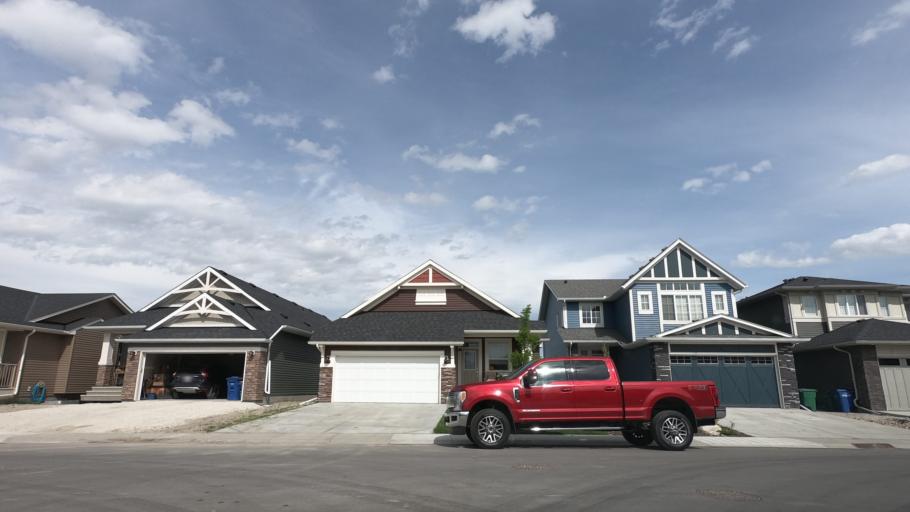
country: CA
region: Alberta
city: Airdrie
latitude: 51.2744
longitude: -114.0413
